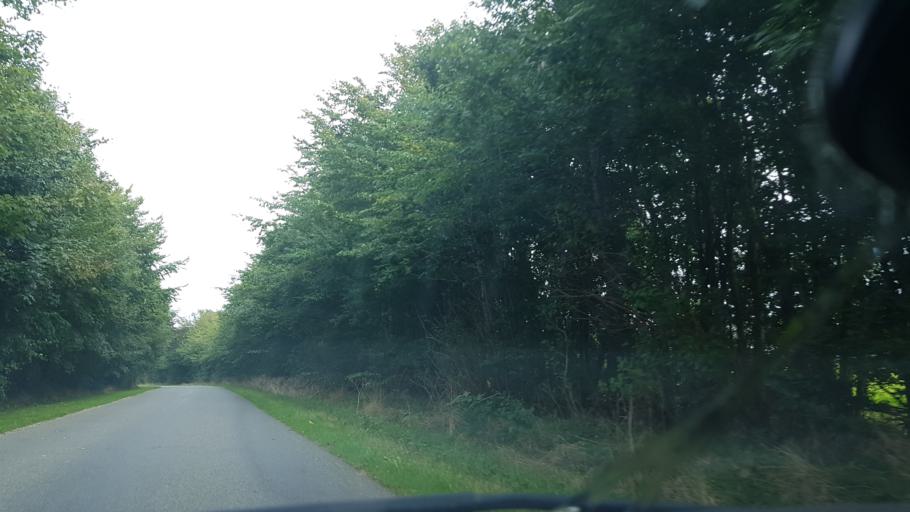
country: DK
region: South Denmark
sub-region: Vejen Kommune
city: Brorup
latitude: 55.4695
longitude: 8.9709
